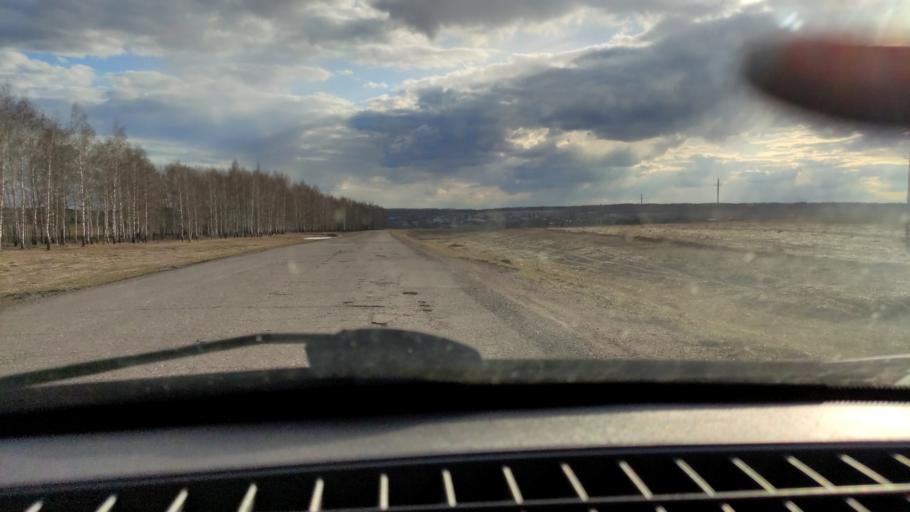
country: RU
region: Bashkortostan
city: Karmaskaly
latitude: 54.3434
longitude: 56.0200
